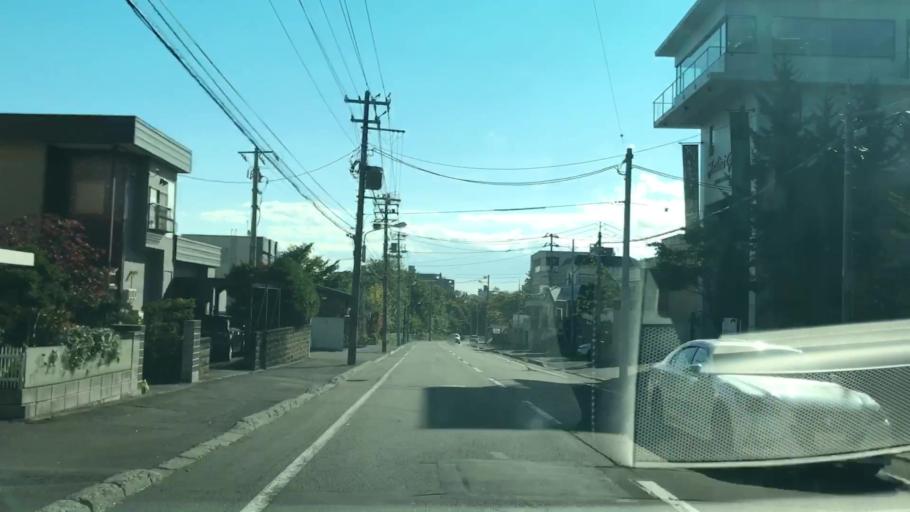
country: JP
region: Hokkaido
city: Sapporo
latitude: 43.0366
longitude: 141.3273
